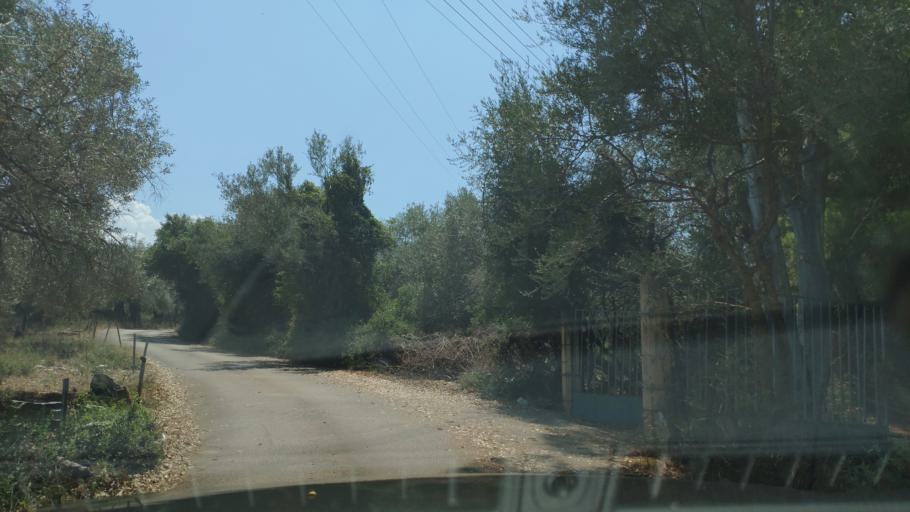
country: GR
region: West Greece
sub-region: Nomos Aitolias kai Akarnanias
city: Amfilochia
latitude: 38.9029
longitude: 21.1175
